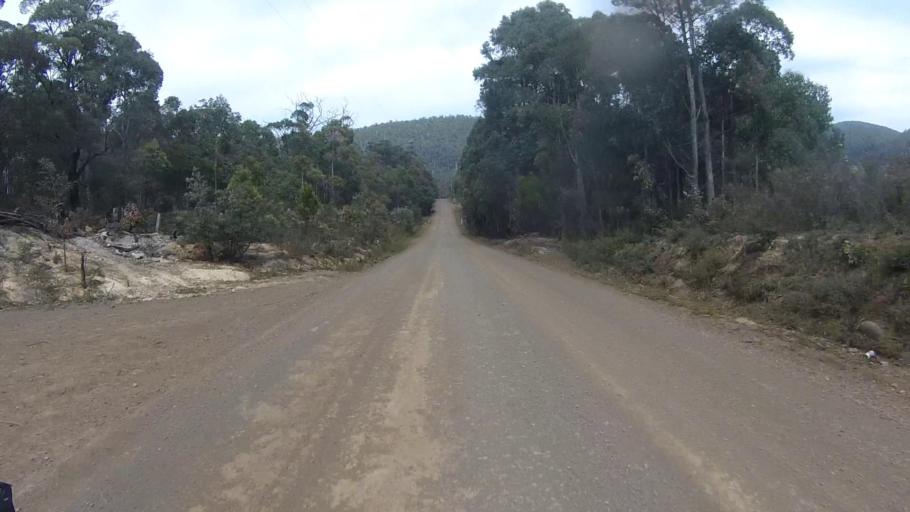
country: AU
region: Tasmania
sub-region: Sorell
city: Sorell
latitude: -42.6874
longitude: 147.8742
